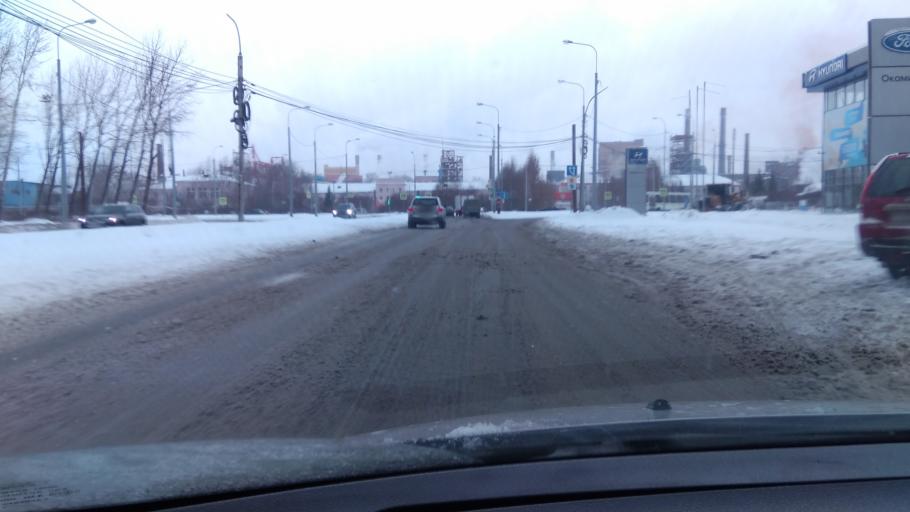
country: RU
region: Sverdlovsk
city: Nizhniy Tagil
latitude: 57.9078
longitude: 60.0092
